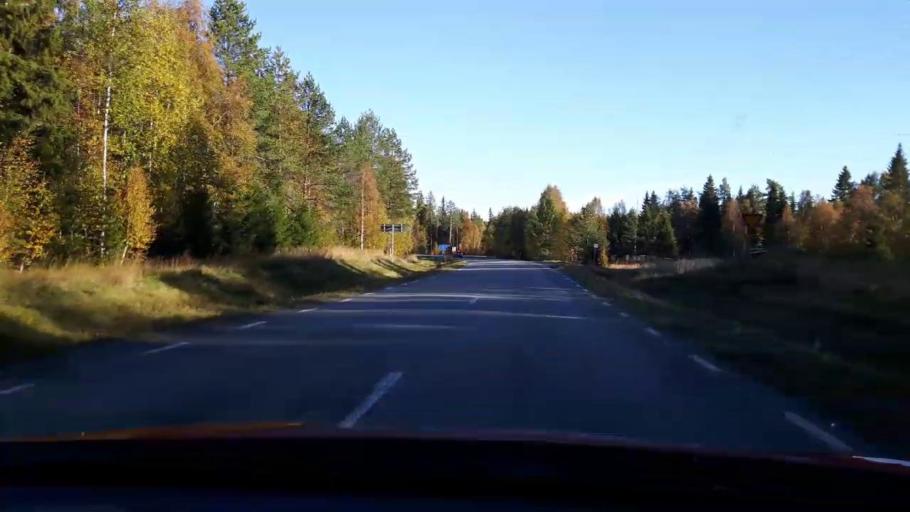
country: SE
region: Jaemtland
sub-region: OEstersunds Kommun
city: Lit
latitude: 63.7372
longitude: 14.7405
